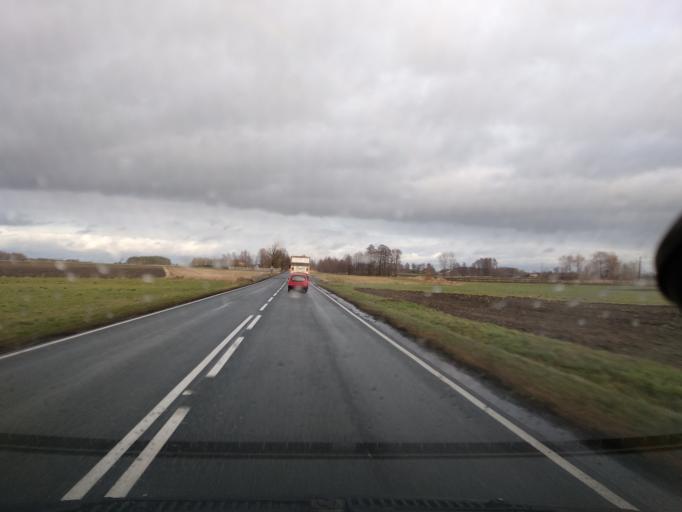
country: PL
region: Greater Poland Voivodeship
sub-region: Powiat koninski
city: Rychwal
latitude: 52.1288
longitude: 18.1786
